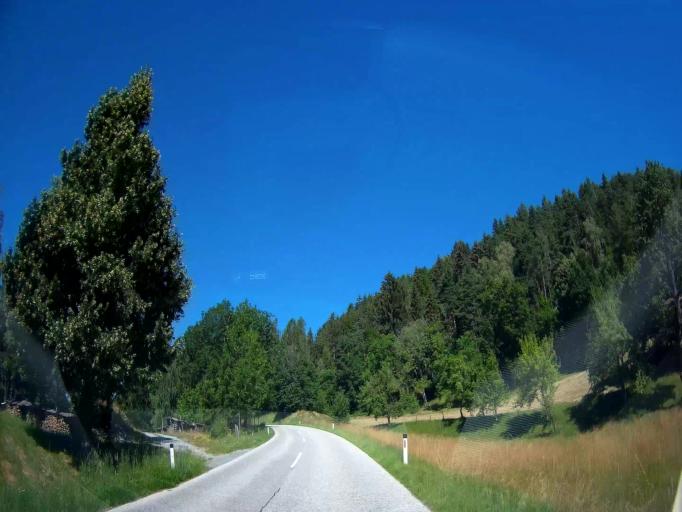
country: AT
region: Carinthia
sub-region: Politischer Bezirk Klagenfurt Land
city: Maria Worth
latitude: 46.6029
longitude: 14.1431
